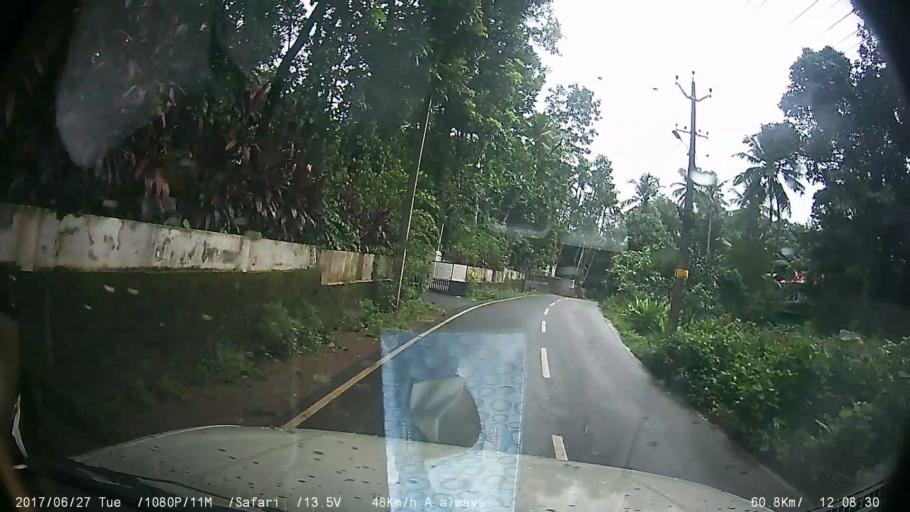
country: IN
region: Kerala
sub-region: Kottayam
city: Palackattumala
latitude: 9.7598
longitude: 76.5566
